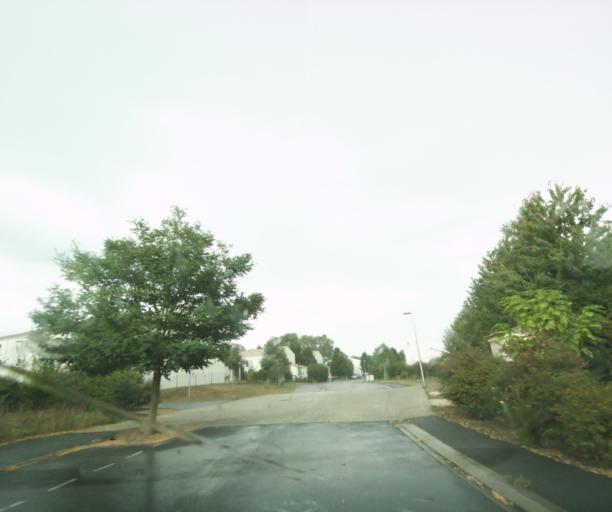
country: FR
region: Poitou-Charentes
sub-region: Departement de la Charente-Maritime
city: Tonnay-Charente
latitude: 45.9493
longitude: -0.8755
